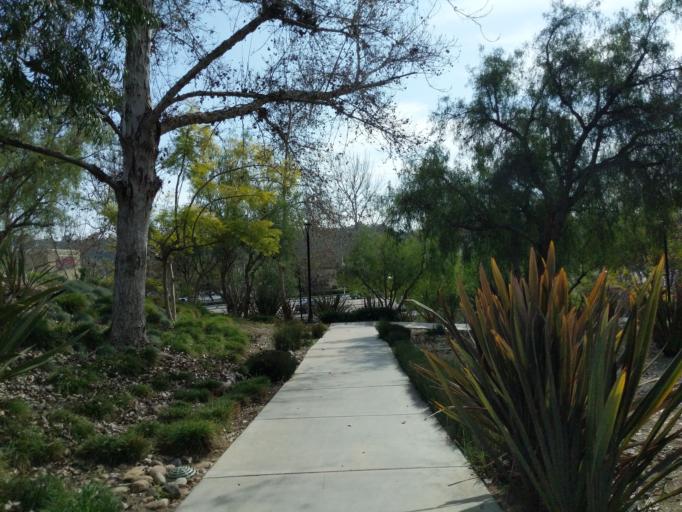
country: US
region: California
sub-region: San Diego County
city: San Diego
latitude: 32.7832
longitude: -117.1304
